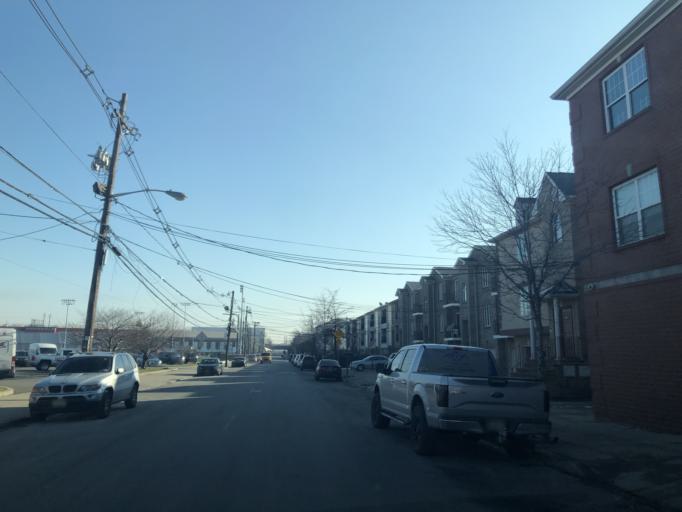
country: US
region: New Jersey
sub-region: Hudson County
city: Harrison
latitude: 40.7286
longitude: -74.1457
